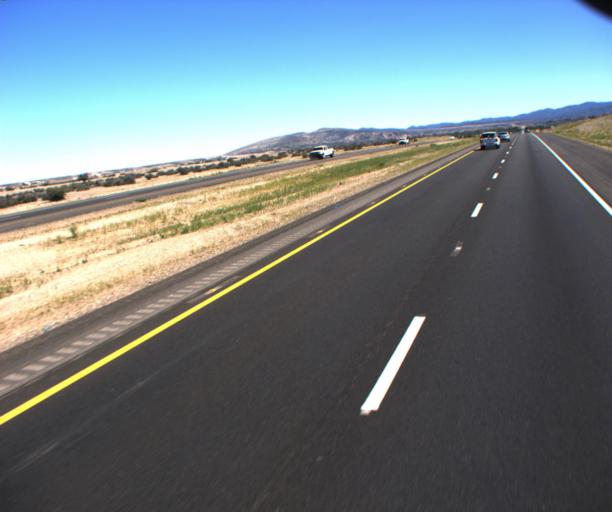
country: US
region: Arizona
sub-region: Yavapai County
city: Chino Valley
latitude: 34.6665
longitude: -112.4391
